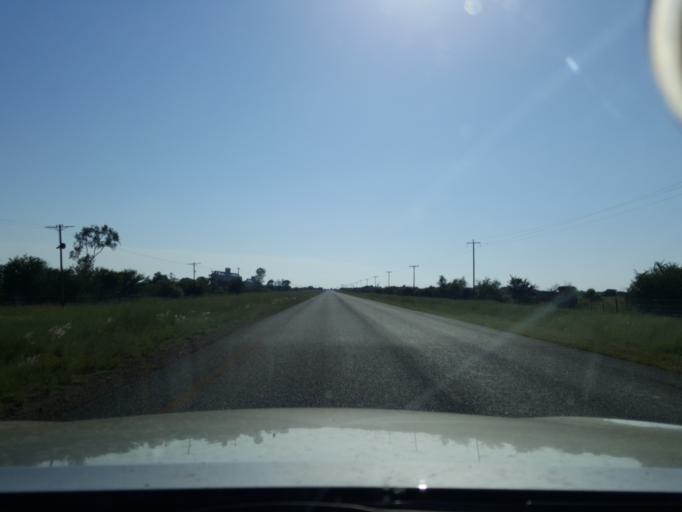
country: ZA
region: North-West
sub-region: Ngaka Modiri Molema District Municipality
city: Mahikeng
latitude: -25.8321
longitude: 25.7798
